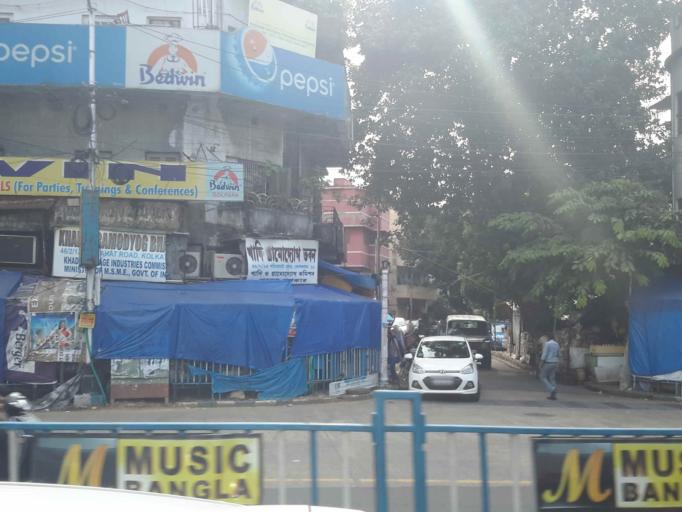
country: IN
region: West Bengal
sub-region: Kolkata
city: Kolkata
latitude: 22.5170
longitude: 88.3662
